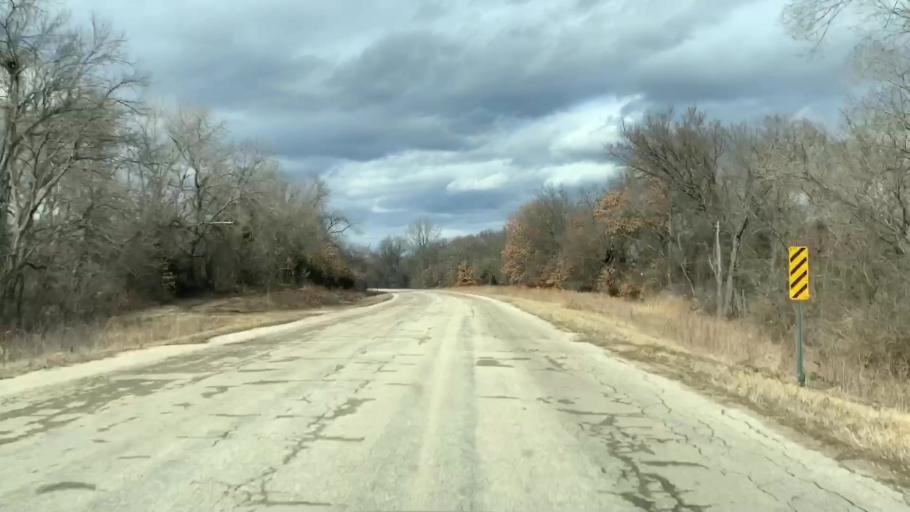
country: US
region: Kansas
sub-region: Allen County
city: Humboldt
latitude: 37.7488
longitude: -95.4703
